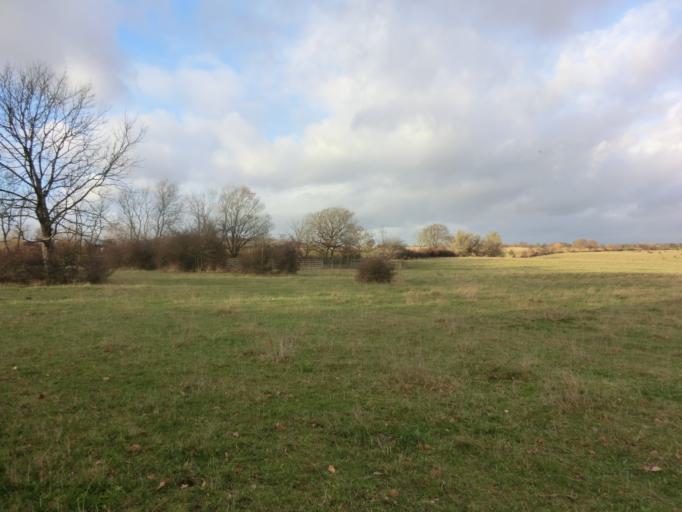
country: SE
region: Skane
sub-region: Lunds Kommun
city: Genarp
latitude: 55.6789
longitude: 13.3300
